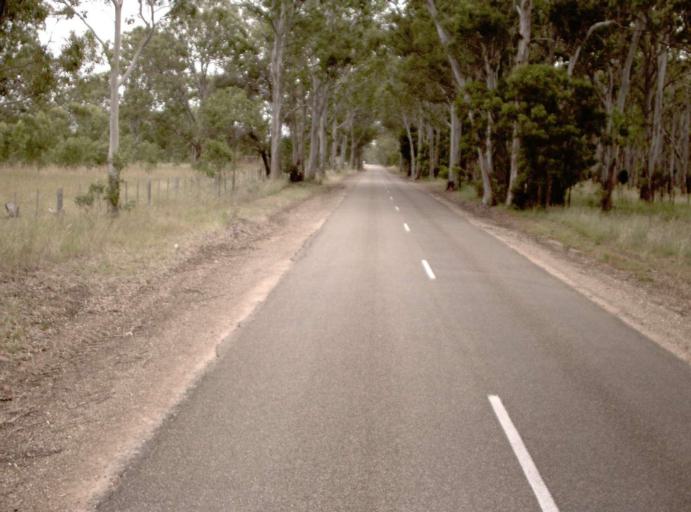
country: AU
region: Victoria
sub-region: Wellington
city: Sale
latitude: -37.8620
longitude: 147.0690
